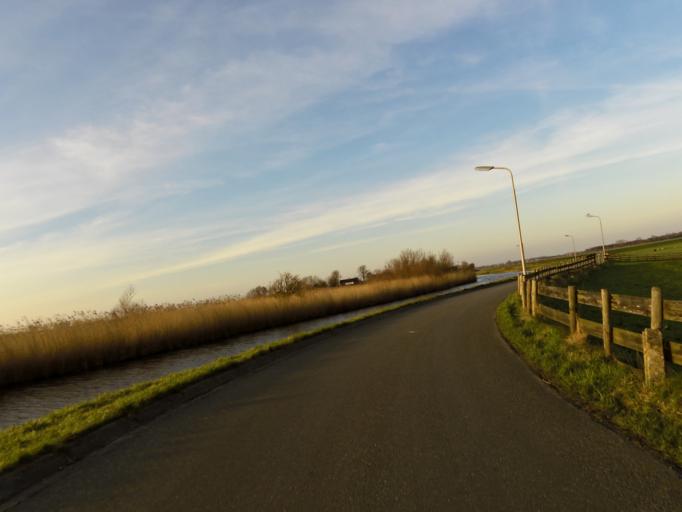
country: NL
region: South Holland
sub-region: Gemeente Leiderdorp
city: Leiderdorp
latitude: 52.1915
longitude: 4.5585
